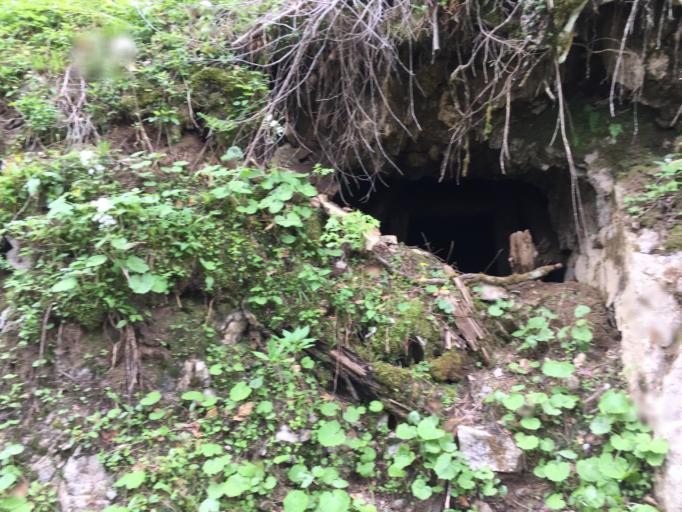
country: IT
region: Friuli Venezia Giulia
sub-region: Provincia di Udine
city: Pontebba
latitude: 46.5147
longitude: 13.2411
